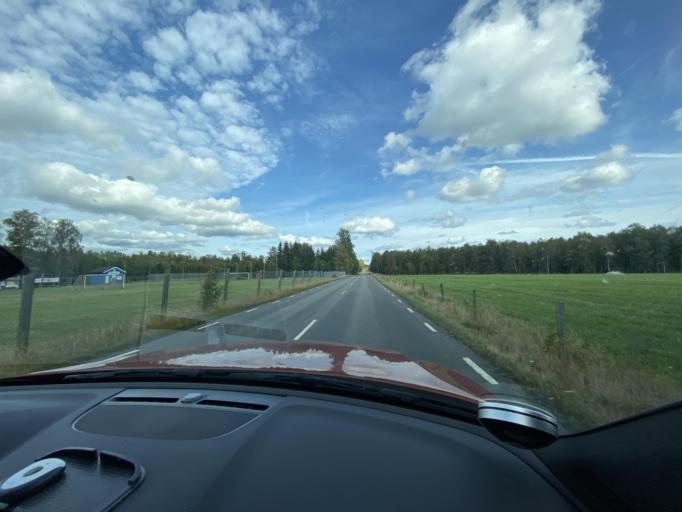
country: SE
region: Skane
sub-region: Hassleholms Kommun
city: Bjarnum
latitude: 56.3579
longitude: 13.7871
